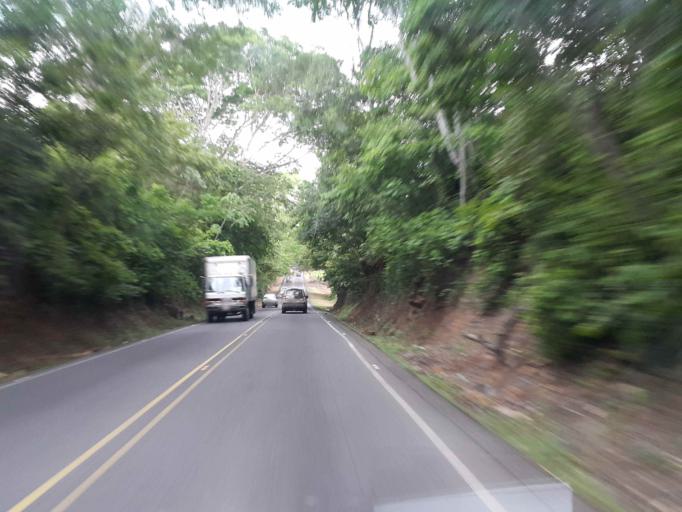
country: CR
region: Puntarenas
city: Miramar
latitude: 10.0882
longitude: -84.7929
